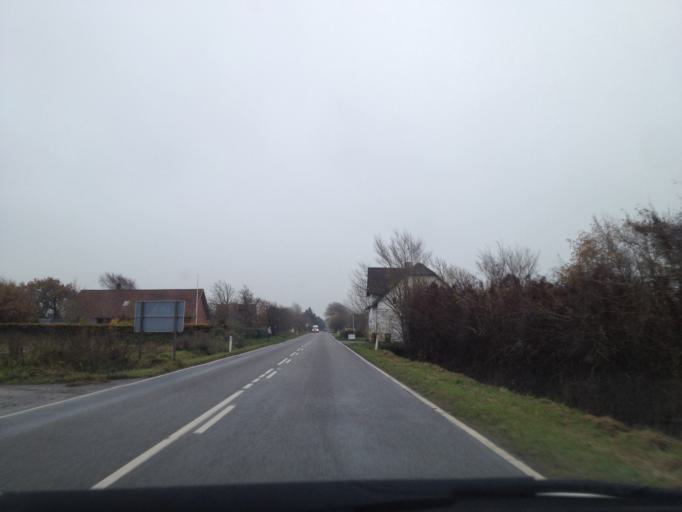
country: DK
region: South Denmark
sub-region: Tonder Kommune
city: Sherrebek
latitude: 55.0833
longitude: 8.7259
